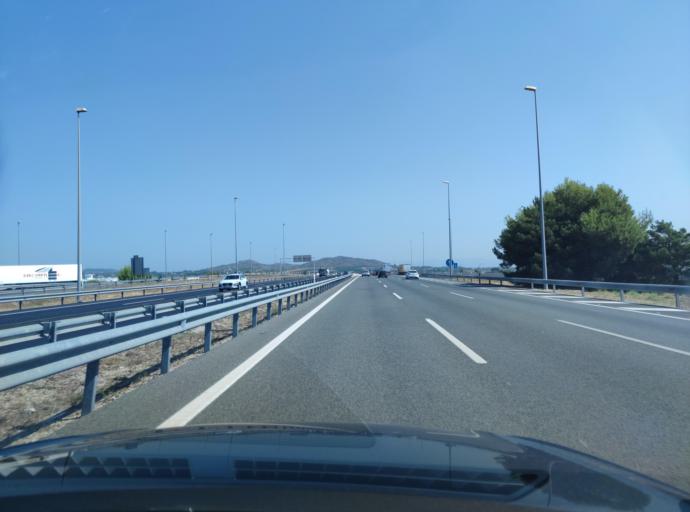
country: ES
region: Valencia
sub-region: Provincia de Valencia
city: Ribarroja
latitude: 39.4742
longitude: -0.5491
